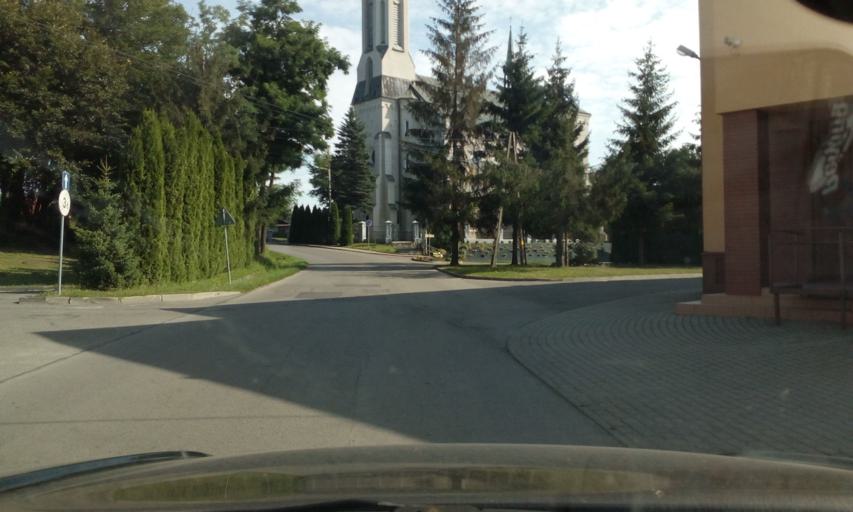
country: PL
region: Subcarpathian Voivodeship
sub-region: Powiat lancucki
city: Wysoka
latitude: 50.0441
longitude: 22.2494
